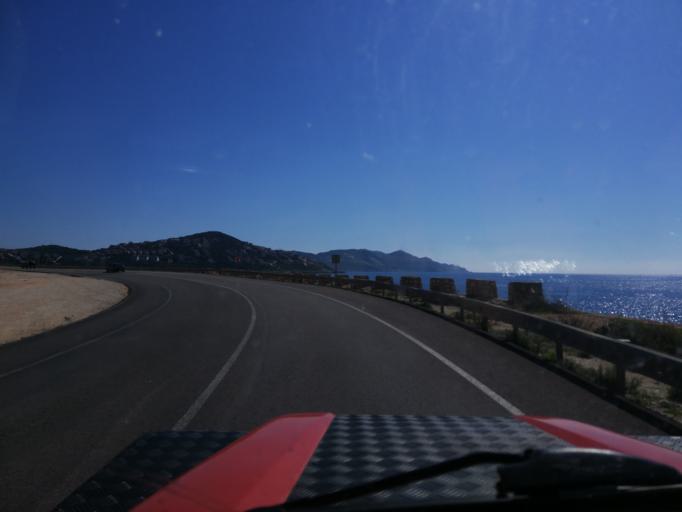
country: TR
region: Antalya
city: Kas
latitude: 36.2030
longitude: 29.5839
